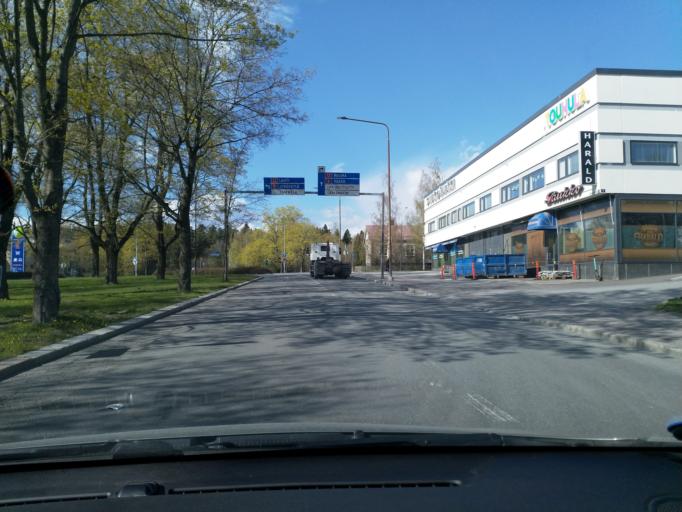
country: FI
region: Pirkanmaa
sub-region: Tampere
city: Tampere
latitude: 61.5044
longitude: 23.7870
